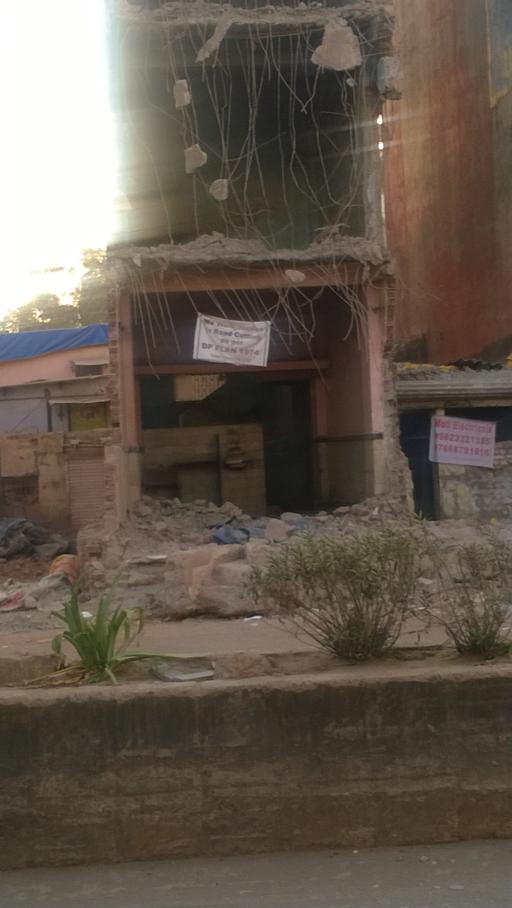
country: IN
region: Maharashtra
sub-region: Thane
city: Ulhasnagar
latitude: 19.2293
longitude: 73.1587
